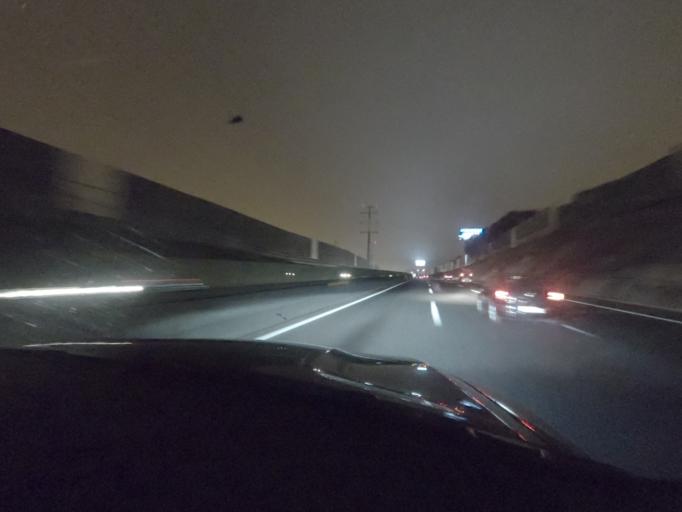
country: PT
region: Lisbon
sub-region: Loures
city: Santa Iria da Azoia
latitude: 38.8439
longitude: -9.0926
